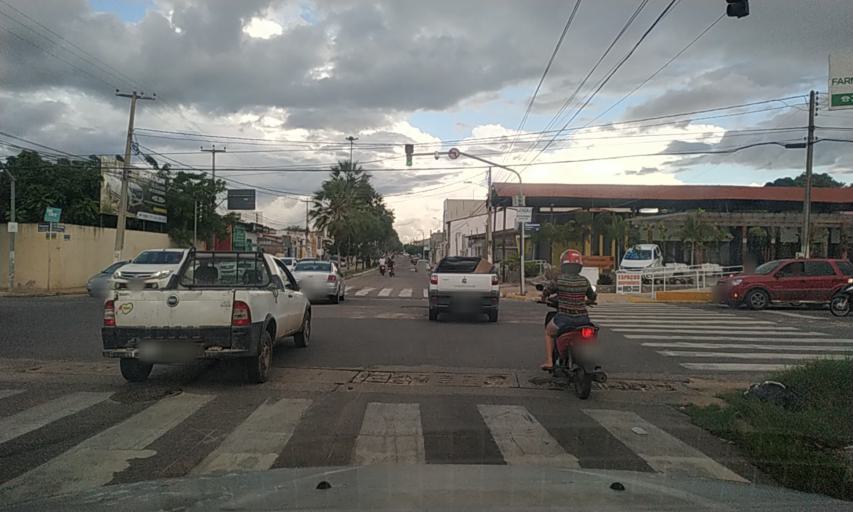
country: BR
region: Rio Grande do Norte
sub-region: Mossoro
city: Mossoro
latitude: -5.1865
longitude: -37.3532
